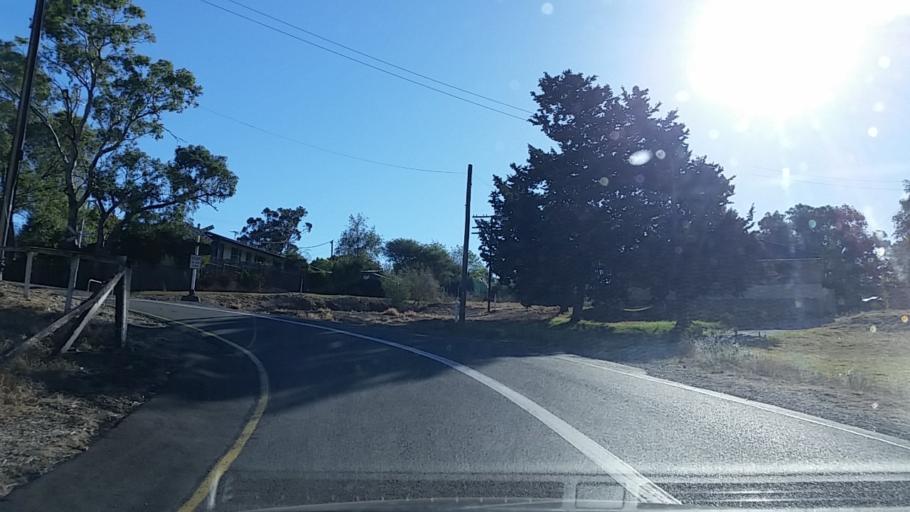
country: AU
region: South Australia
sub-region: Mount Barker
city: Nairne
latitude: -35.0387
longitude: 138.9175
